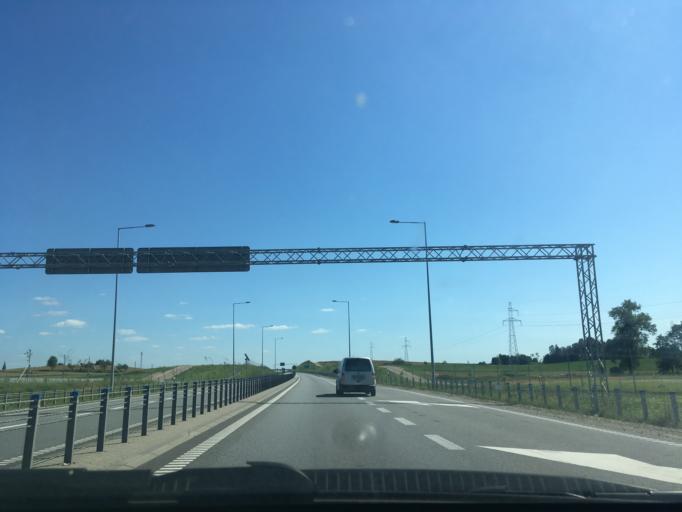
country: PL
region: Podlasie
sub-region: Powiat suwalski
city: Raczki
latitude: 53.9108
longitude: 22.8390
